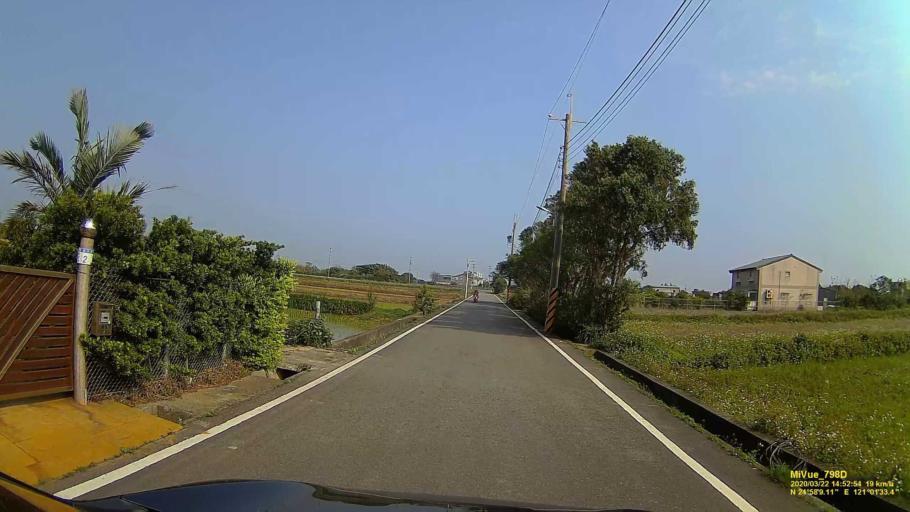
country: TW
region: Taiwan
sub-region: Hsinchu
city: Zhubei
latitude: 24.9691
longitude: 121.0260
